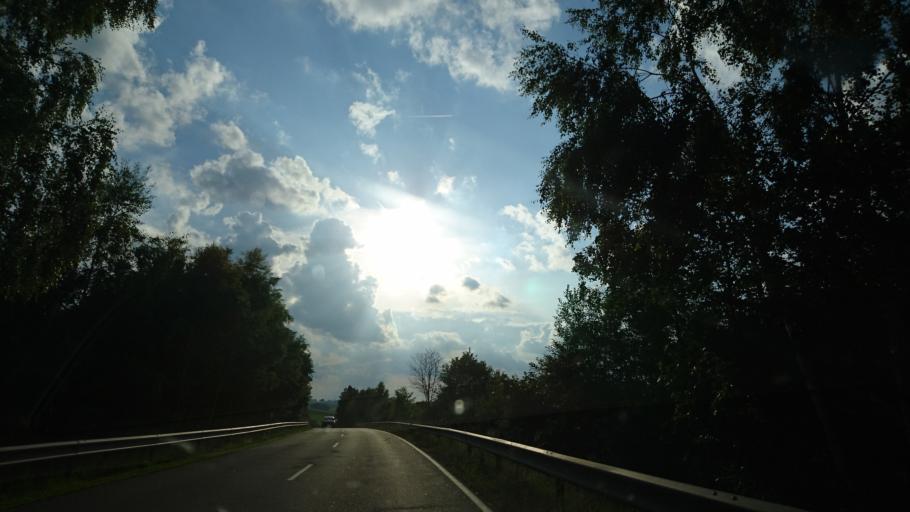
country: DE
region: Bavaria
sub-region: Lower Bavaria
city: Grafenau
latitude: 48.8752
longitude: 13.4105
